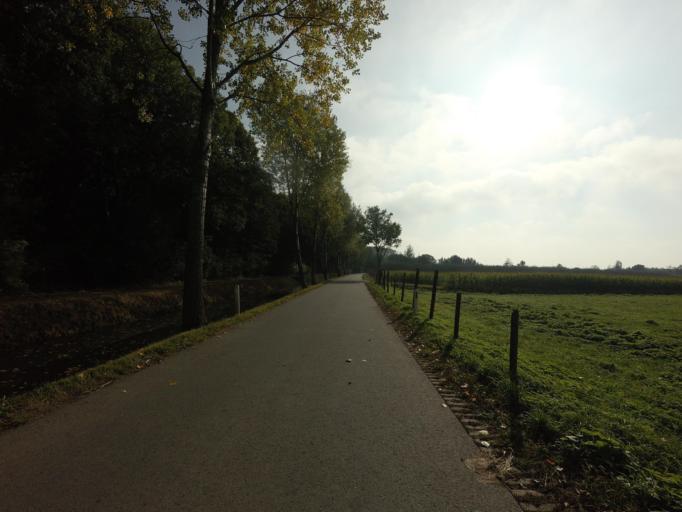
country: NL
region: Utrecht
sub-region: Gemeente Vianen
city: Vianen
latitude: 51.9710
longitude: 5.0910
